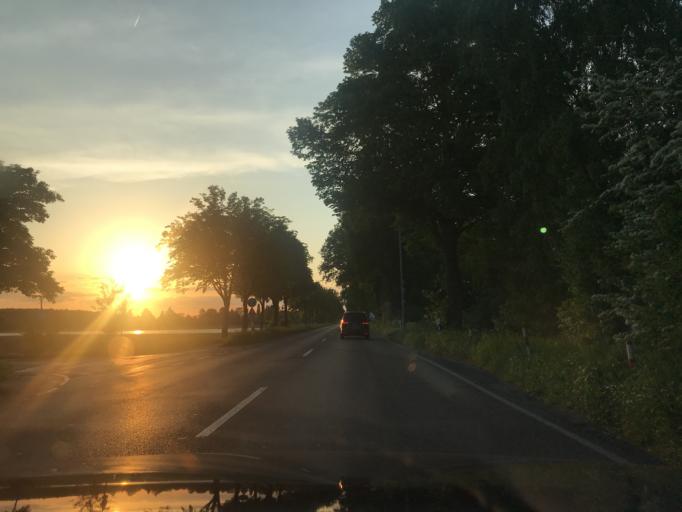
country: DE
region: North Rhine-Westphalia
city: Tonisvorst
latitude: 51.3019
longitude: 6.5276
